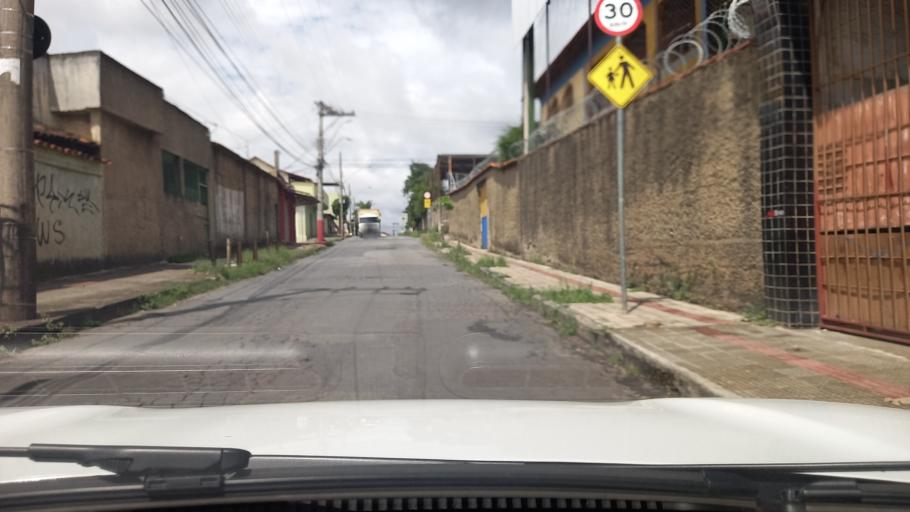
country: BR
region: Minas Gerais
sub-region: Contagem
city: Contagem
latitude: -19.8997
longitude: -44.0251
